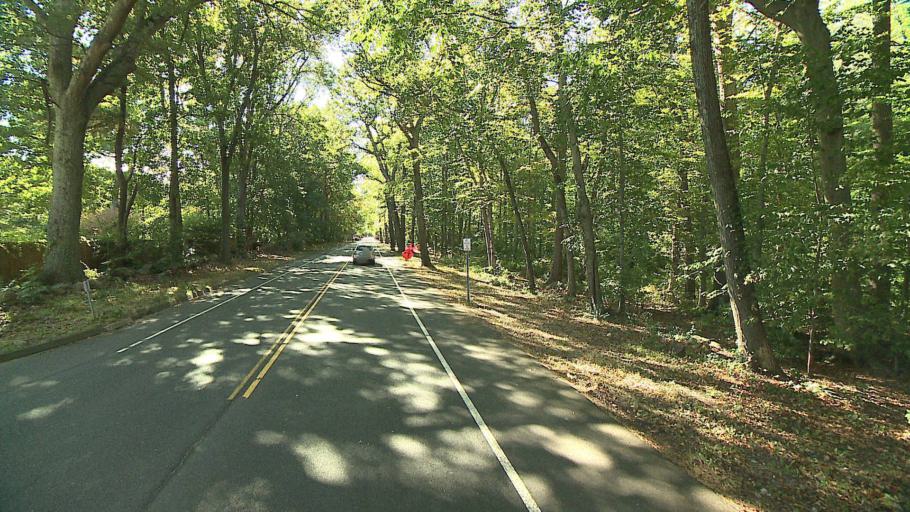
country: US
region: Connecticut
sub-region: Fairfield County
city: New Canaan
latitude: 41.1264
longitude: -73.4854
